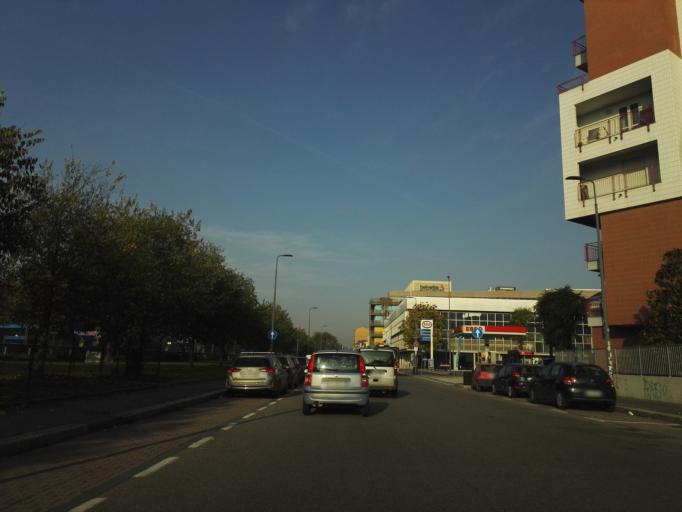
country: IT
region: Lombardy
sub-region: Citta metropolitana di Milano
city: Chiaravalle
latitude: 45.4357
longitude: 9.2336
